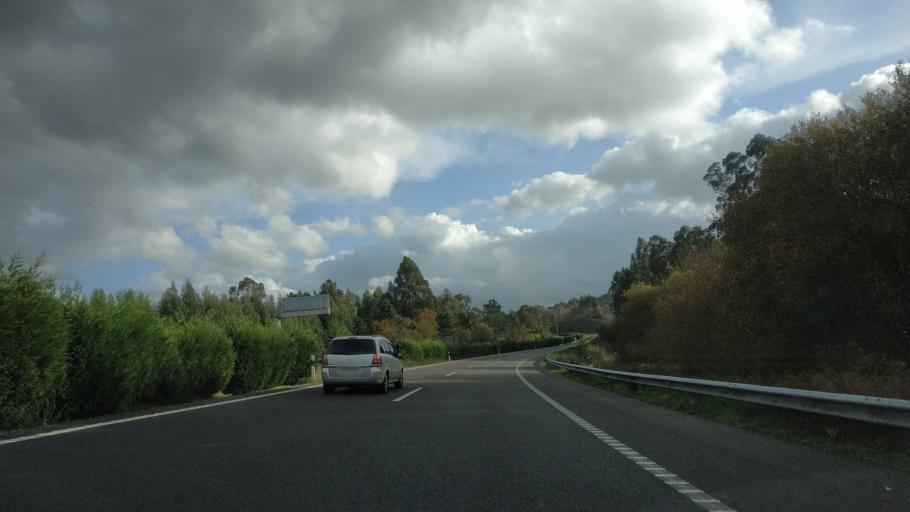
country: ES
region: Galicia
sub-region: Provincia da Coruna
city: Cambre
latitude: 43.2684
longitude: -8.3571
